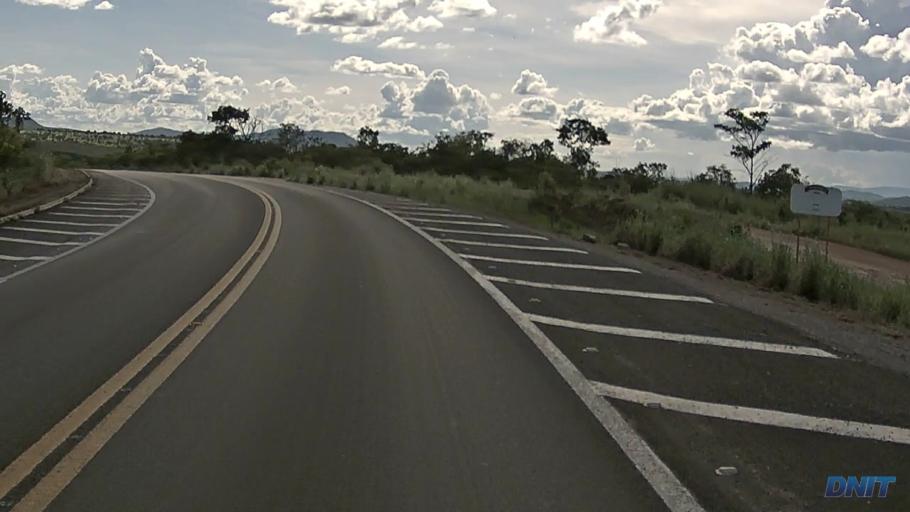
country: BR
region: Goias
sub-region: Padre Bernardo
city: Padre Bernardo
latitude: -15.2100
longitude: -48.5676
